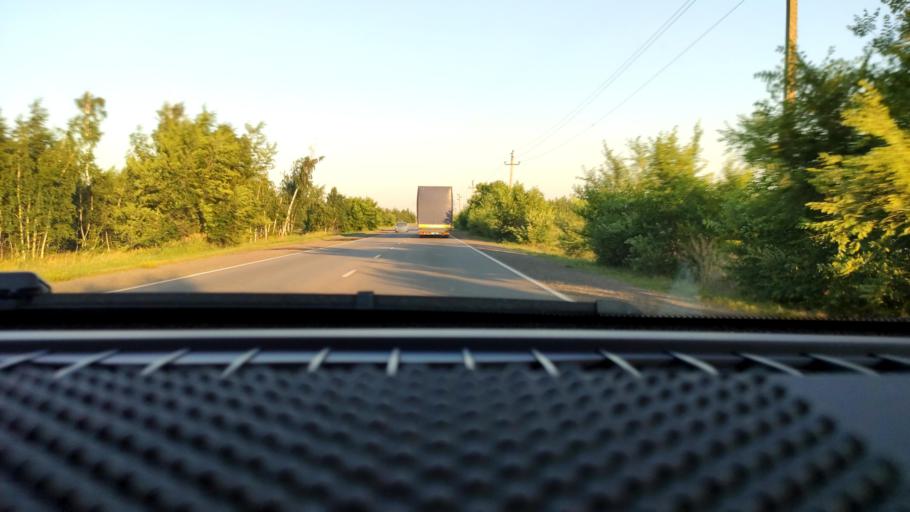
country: RU
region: Voronezj
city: Maslovka
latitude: 51.5808
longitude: 39.2626
